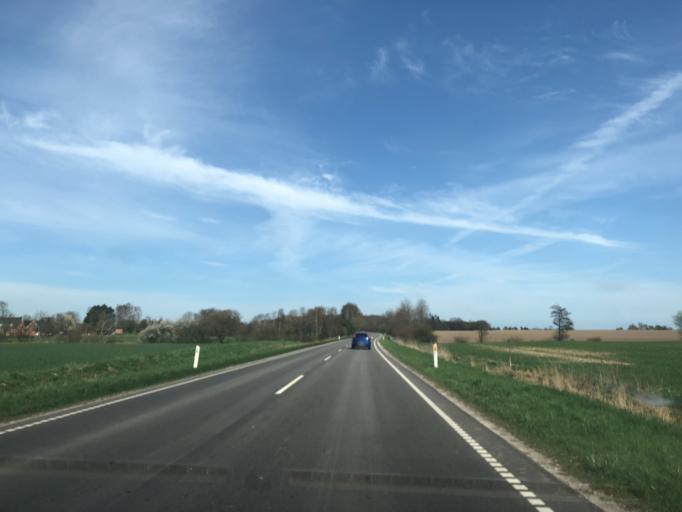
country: DK
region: Zealand
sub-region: Faxe Kommune
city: Fakse
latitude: 55.2772
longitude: 12.1597
